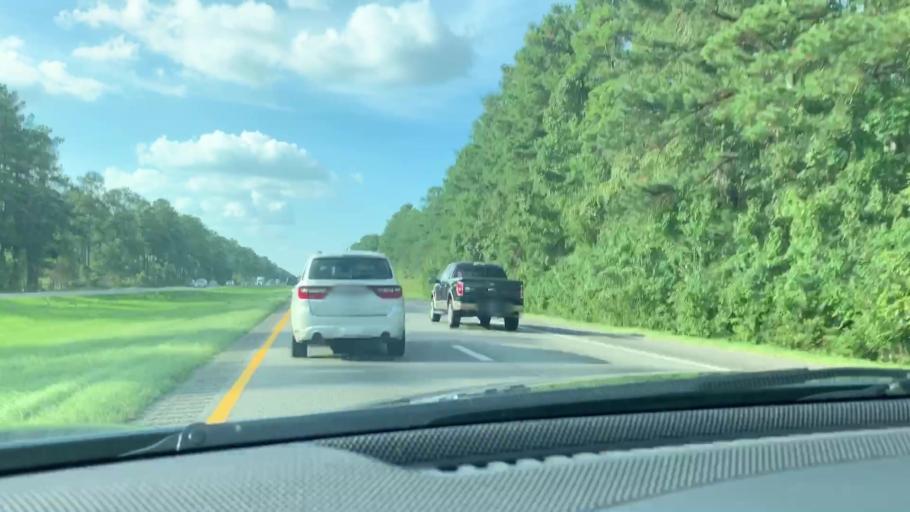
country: US
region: South Carolina
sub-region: Orangeburg County
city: Brookdale
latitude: 33.5379
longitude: -80.8068
